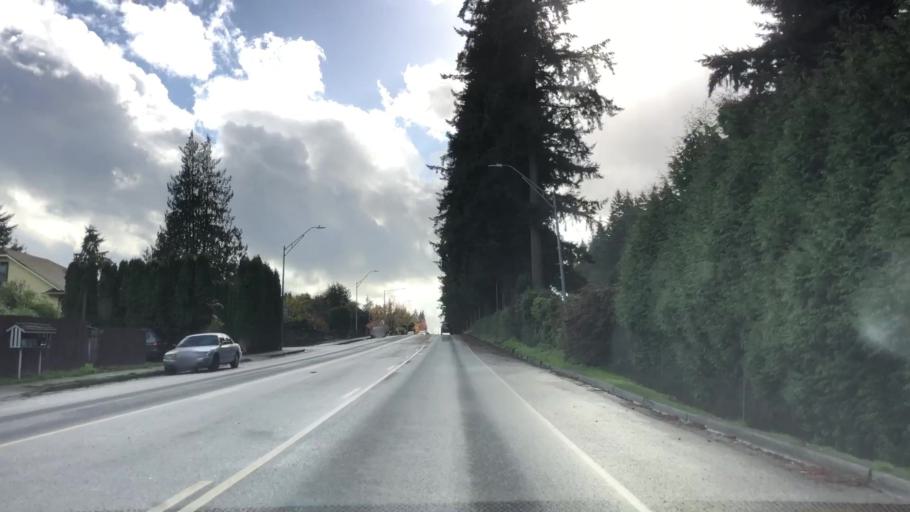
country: US
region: Washington
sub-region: Snohomish County
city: Everett
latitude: 47.9484
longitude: -122.2066
